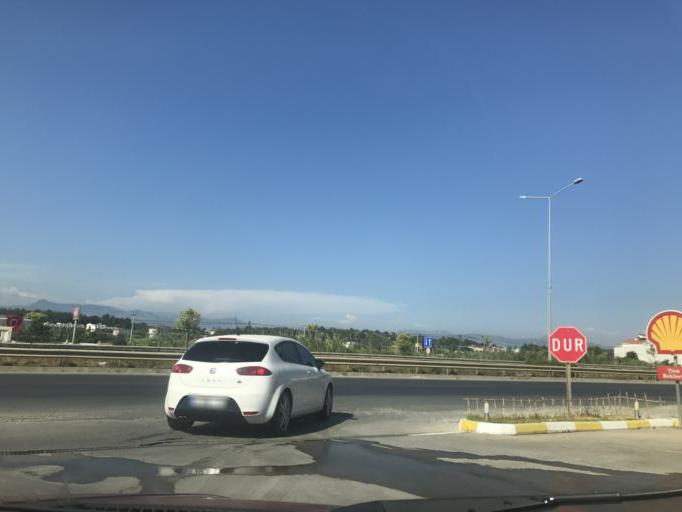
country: TR
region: Antalya
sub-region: Manavgat
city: Side
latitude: 36.8113
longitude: 31.3758
